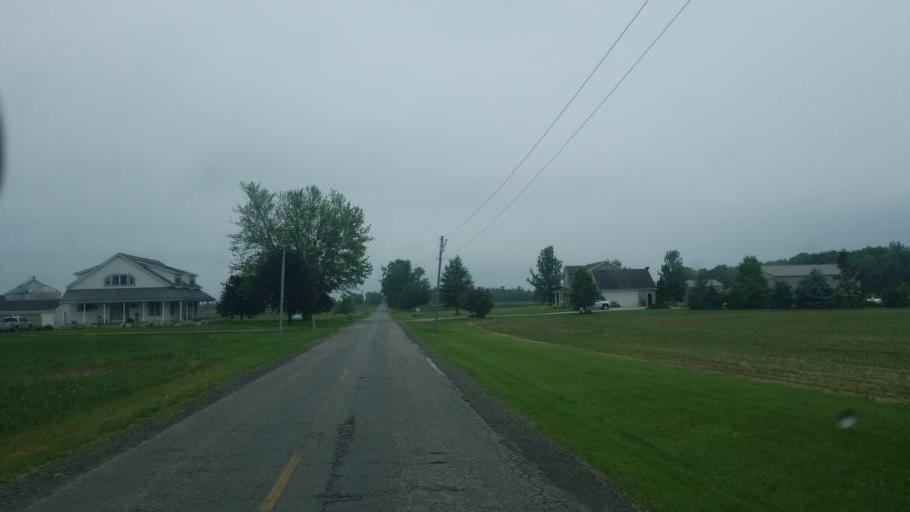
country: US
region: Indiana
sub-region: Marshall County
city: Bremen
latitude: 41.5038
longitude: -86.1179
